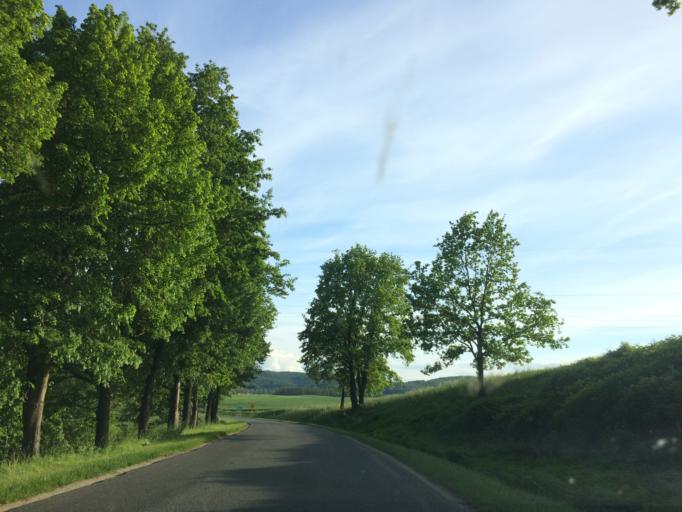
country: PL
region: Lower Silesian Voivodeship
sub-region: Powiat swidnicki
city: Swidnica
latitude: 50.7892
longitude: 16.5004
